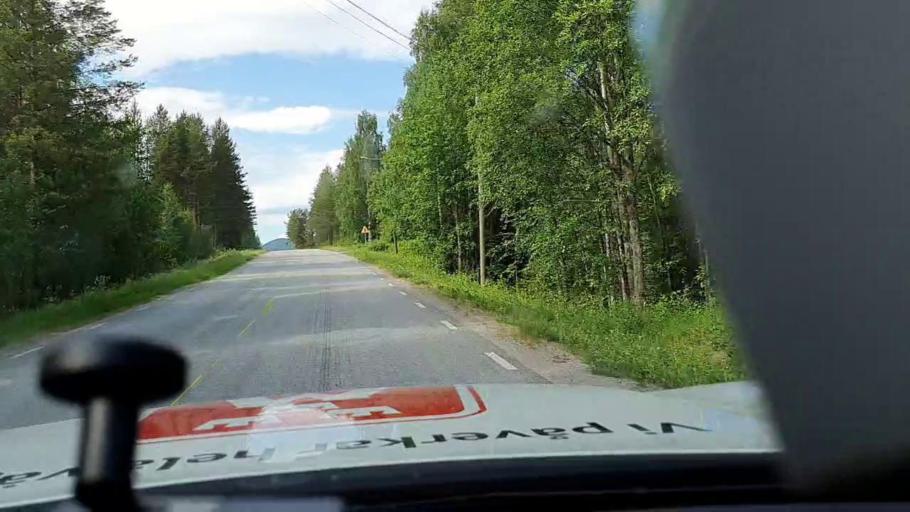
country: SE
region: Norrbotten
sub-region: Gallivare Kommun
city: Gaellivare
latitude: 66.4554
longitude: 20.6564
